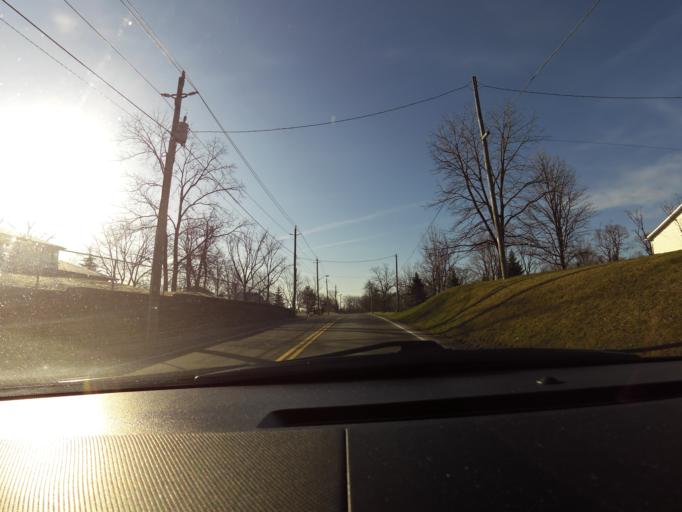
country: CA
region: Ontario
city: Ancaster
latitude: 43.0190
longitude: -79.8892
